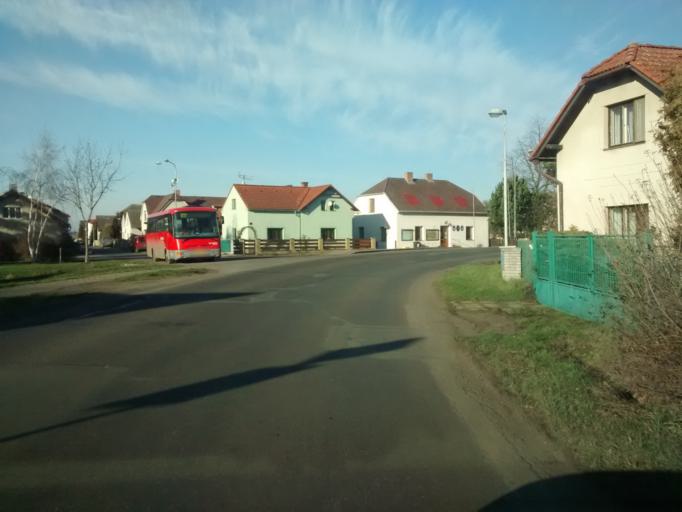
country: CZ
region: Central Bohemia
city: Dobrovice
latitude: 50.4070
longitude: 15.0030
